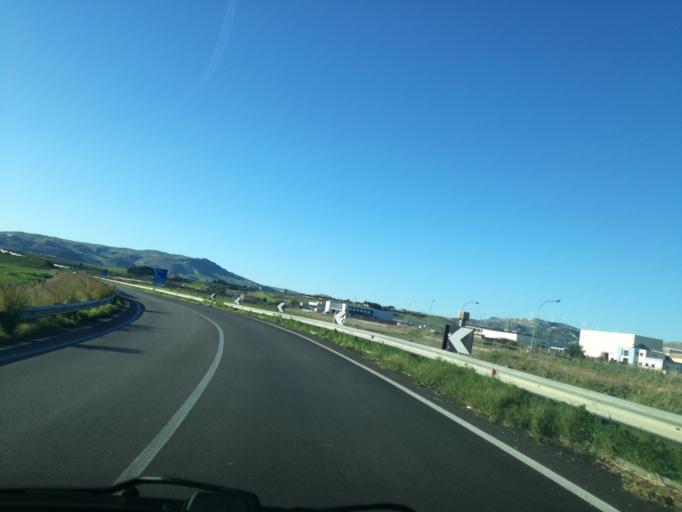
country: IT
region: Sicily
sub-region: Provincia di Caltanissetta
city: Butera
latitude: 37.1238
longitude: 14.1256
